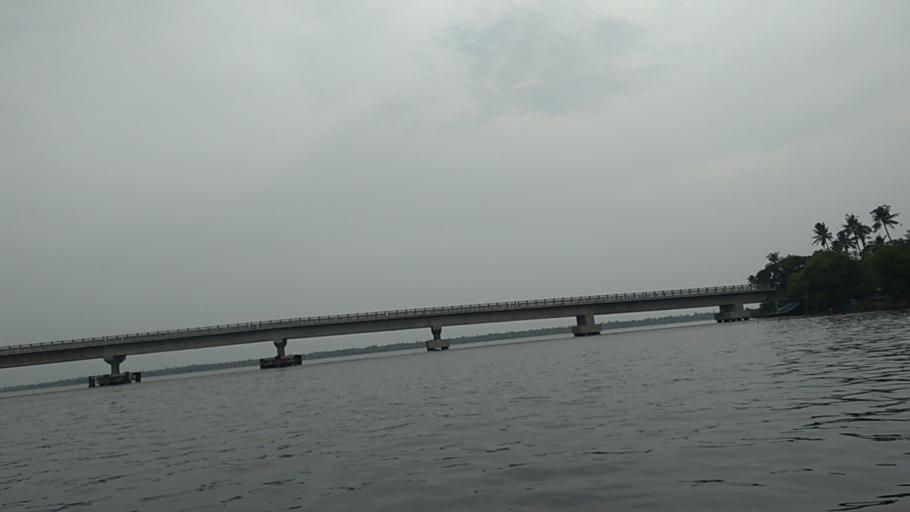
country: IN
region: Kerala
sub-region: Ernakulam
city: Elur
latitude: 10.0744
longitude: 76.2426
